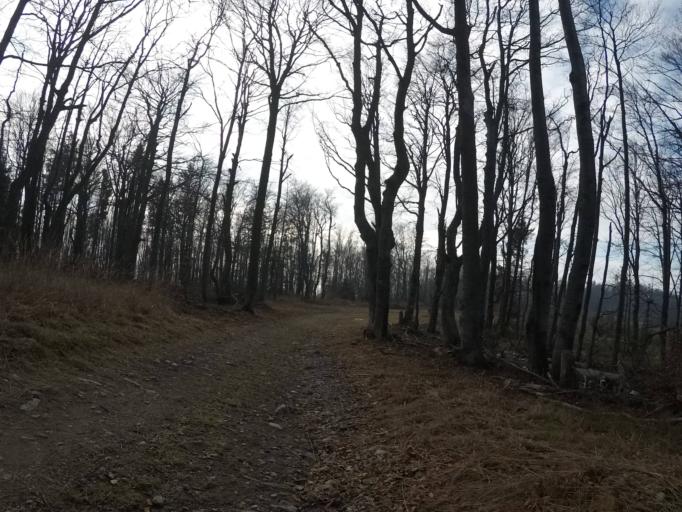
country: SK
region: Kosicky
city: Gelnica
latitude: 48.7764
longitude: 20.9534
